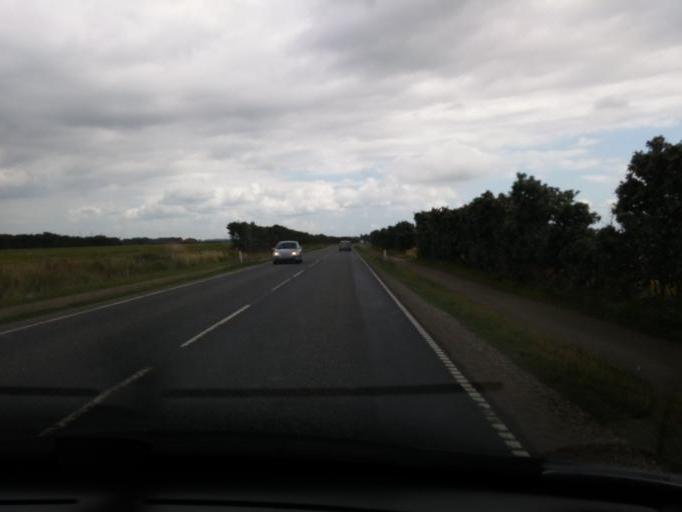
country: DK
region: South Denmark
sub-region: Langeland Kommune
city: Rudkobing
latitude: 54.9591
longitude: 10.6728
